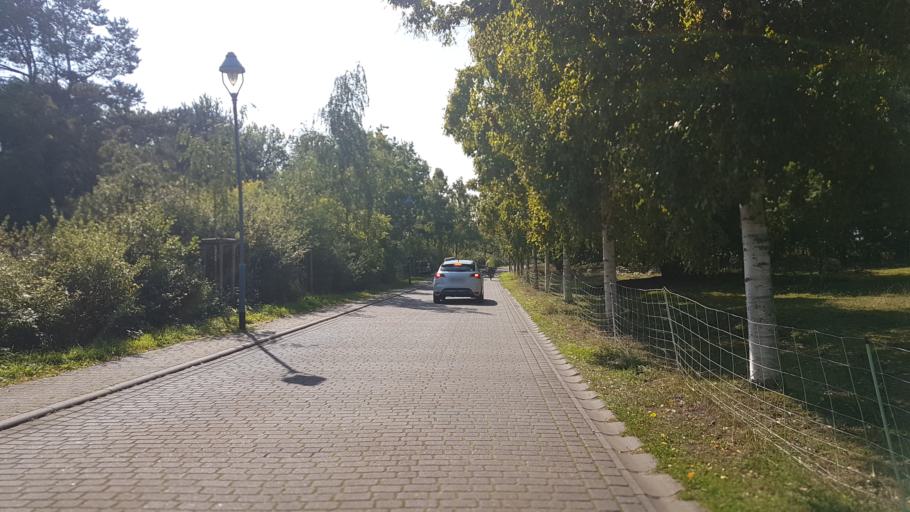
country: DE
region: Mecklenburg-Vorpommern
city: Ostseebad Gohren
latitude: 54.3332
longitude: 13.7324
